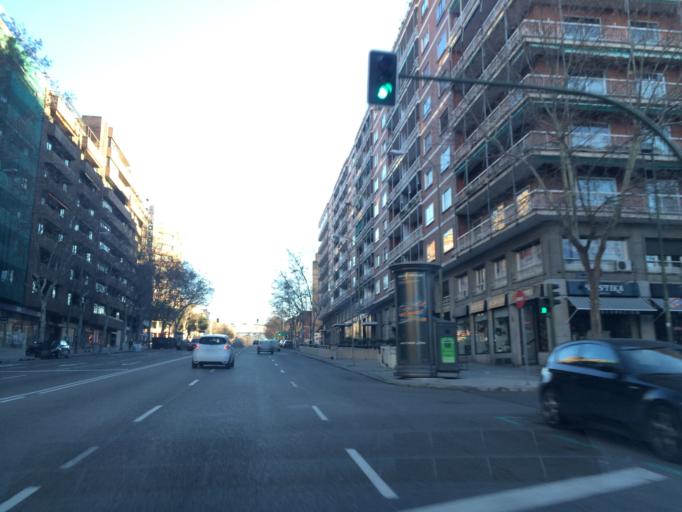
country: ES
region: Madrid
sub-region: Provincia de Madrid
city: Chamberi
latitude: 40.4414
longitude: -3.7143
